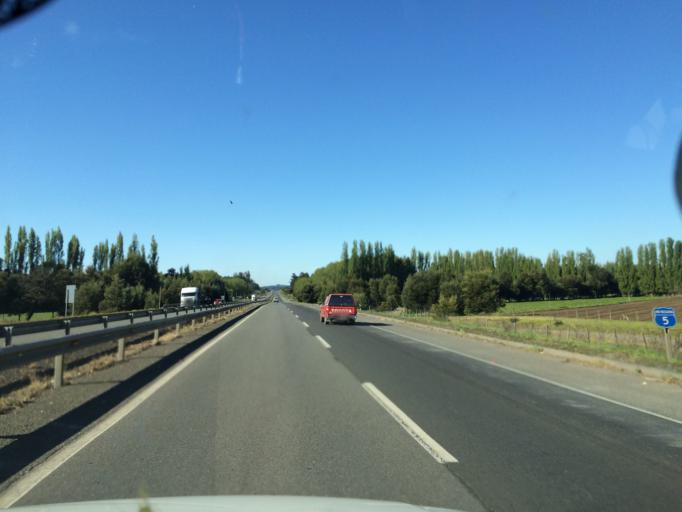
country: CL
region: Biobio
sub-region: Provincia de Biobio
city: Los Angeles
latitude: -37.4358
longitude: -72.3938
